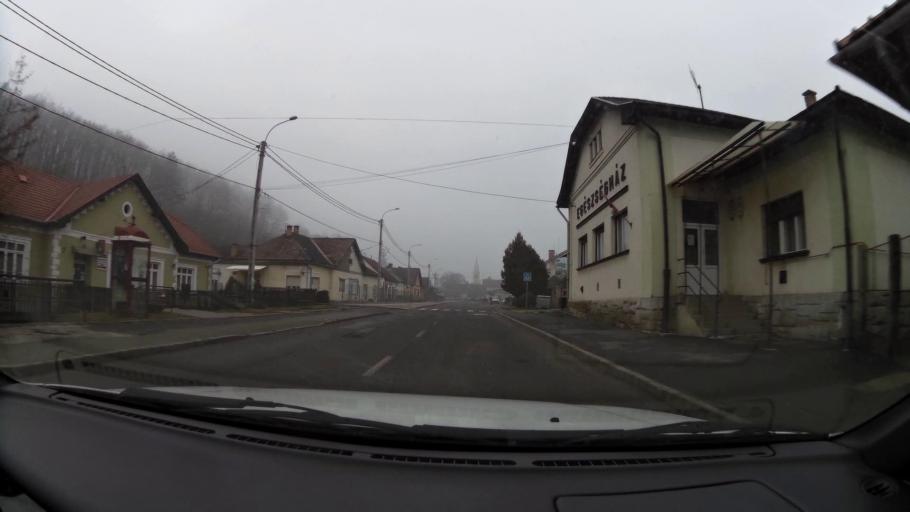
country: HU
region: Borsod-Abauj-Zemplen
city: Rudabanya
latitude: 48.3742
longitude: 20.6215
